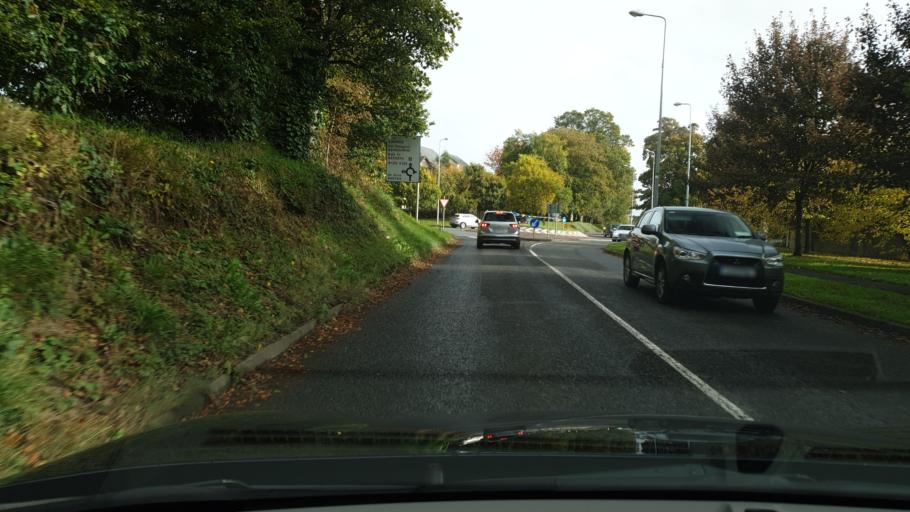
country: IE
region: Leinster
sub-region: An Mhi
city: Ratoath
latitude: 53.5106
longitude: -6.4754
